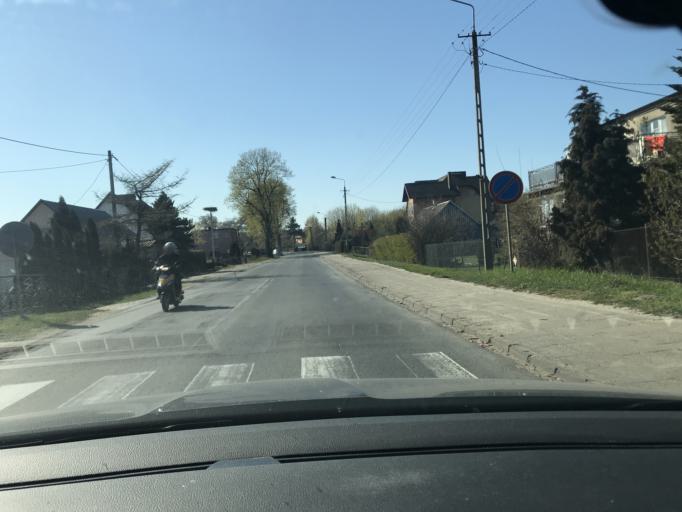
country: PL
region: Pomeranian Voivodeship
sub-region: Powiat nowodworski
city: Sztutowo
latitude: 54.3264
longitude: 19.1676
